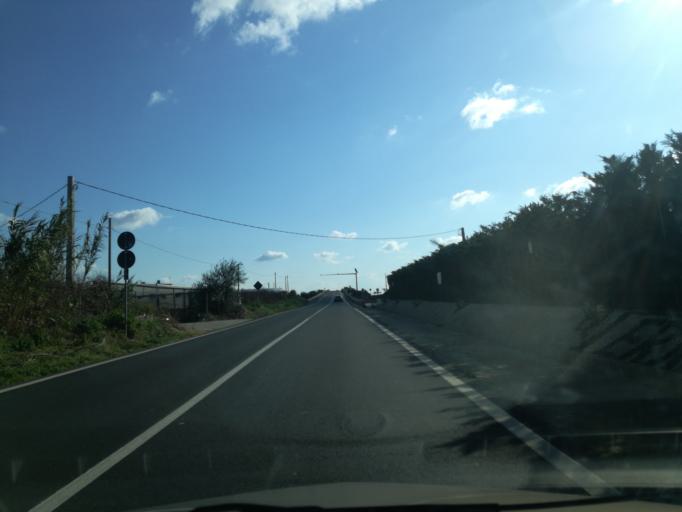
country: IT
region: Sicily
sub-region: Ragusa
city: Acate
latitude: 36.9906
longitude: 14.4415
